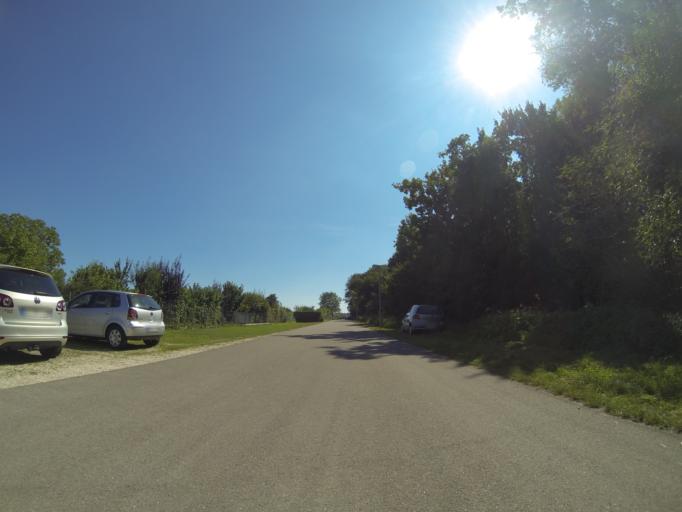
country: DE
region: Baden-Wuerttemberg
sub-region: Tuebingen Region
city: Erbach
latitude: 48.3239
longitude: 9.9036
